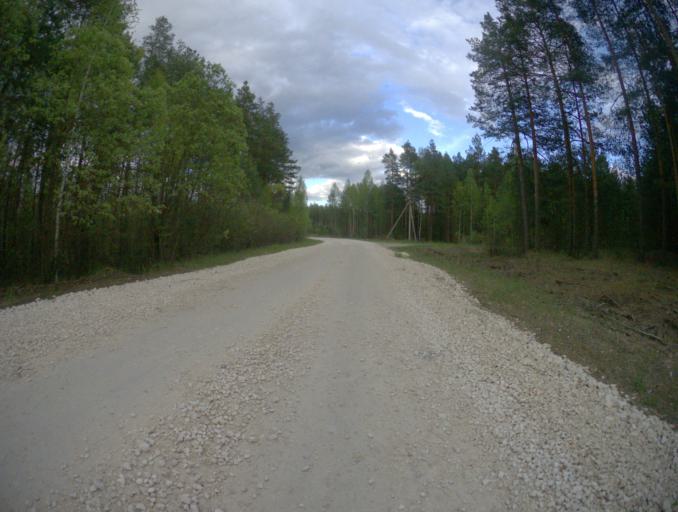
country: RU
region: Vladimir
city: Anopino
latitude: 55.7192
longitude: 40.6046
